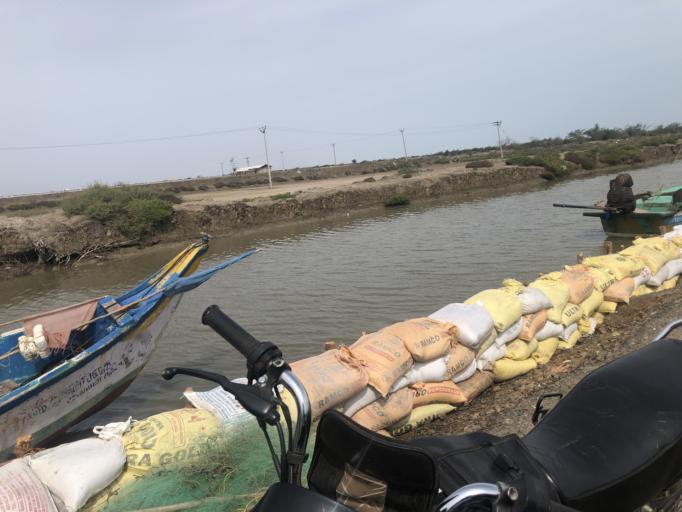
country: IN
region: Tamil Nadu
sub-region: Thanjavur
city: Adirampattinam
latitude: 10.3209
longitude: 79.3796
